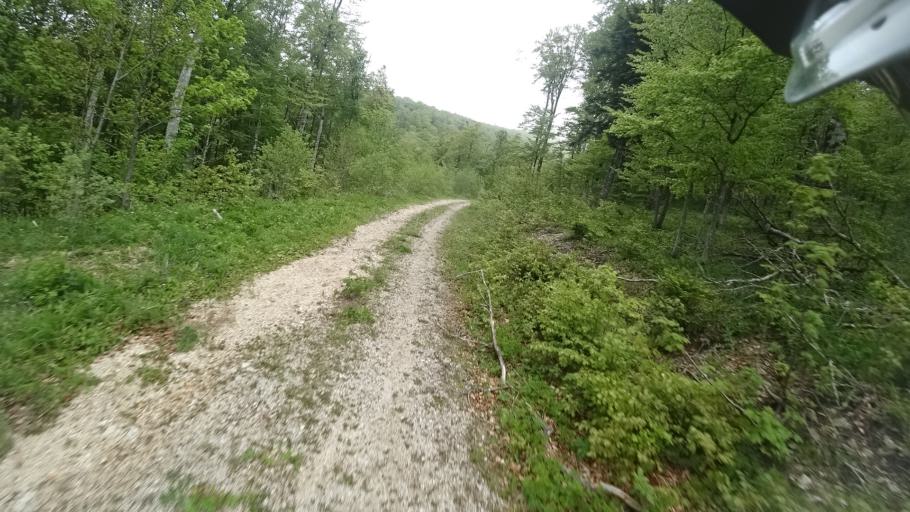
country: BA
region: Federation of Bosnia and Herzegovina
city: Orasac
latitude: 44.5747
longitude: 15.8698
